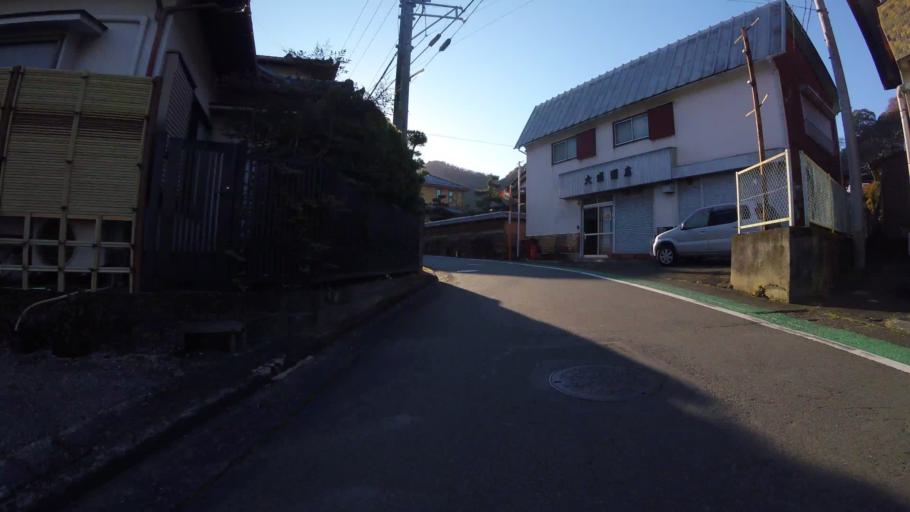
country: JP
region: Shizuoka
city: Mishima
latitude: 34.9890
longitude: 138.9437
